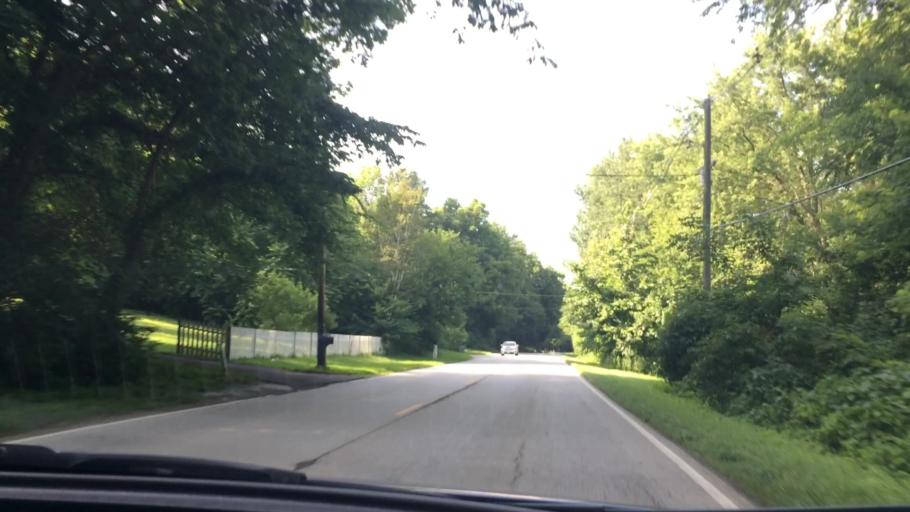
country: US
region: Indiana
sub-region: Tippecanoe County
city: West Lafayette
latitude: 40.4461
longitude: -86.8963
